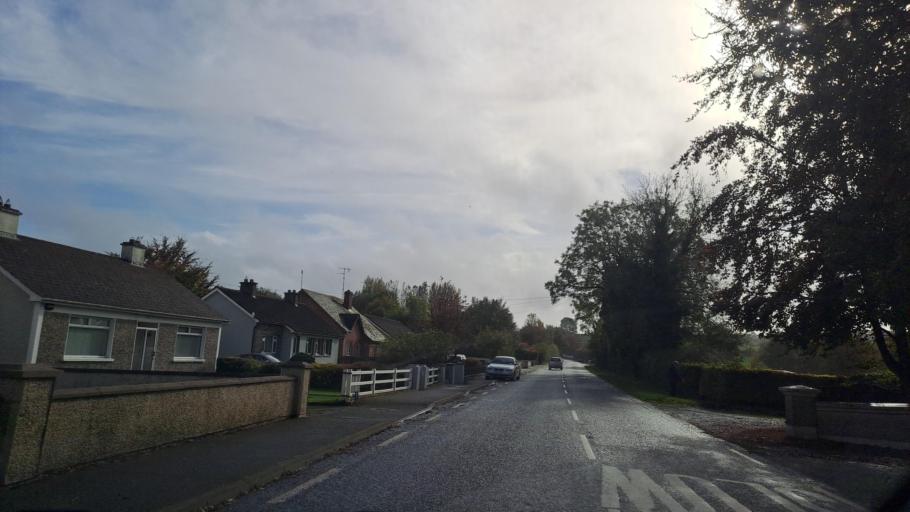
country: IE
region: Ulster
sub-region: County Monaghan
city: Carrickmacross
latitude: 53.9601
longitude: -6.7123
